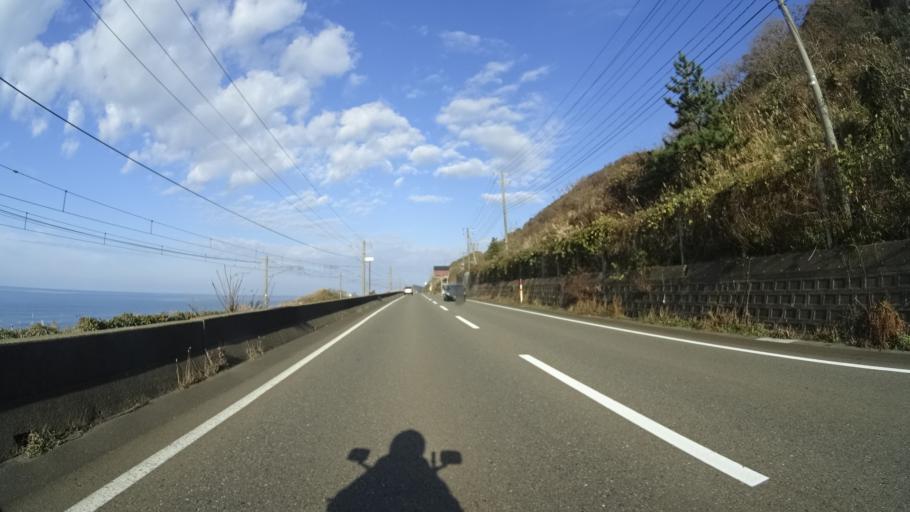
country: JP
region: Niigata
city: Kashiwazaki
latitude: 37.3003
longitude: 138.4123
